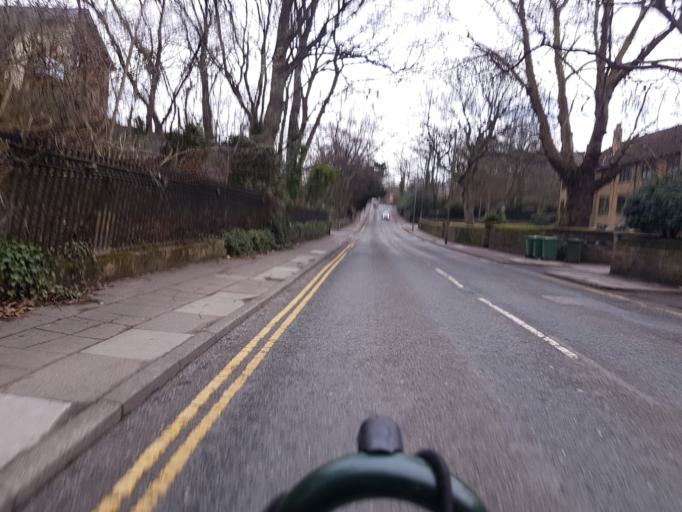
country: GB
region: England
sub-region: Liverpool
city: Liverpool
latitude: 53.3834
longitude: -2.9537
